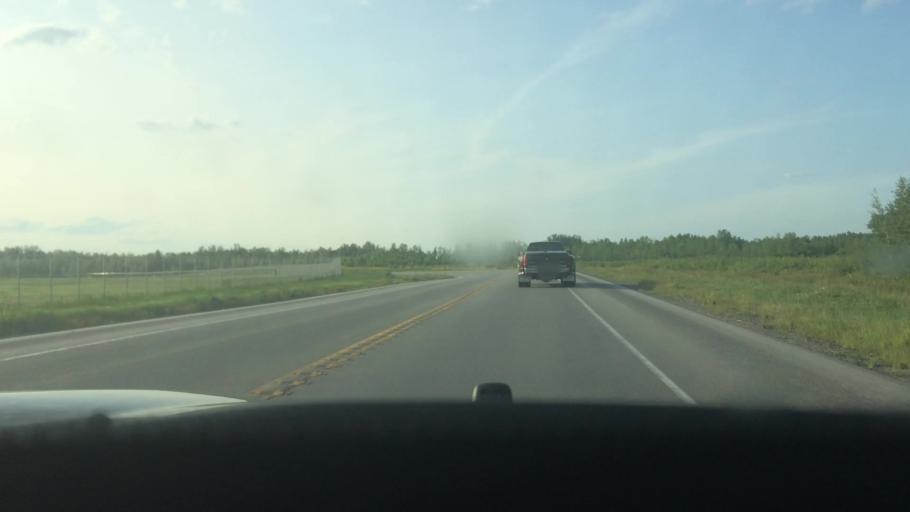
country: US
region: New York
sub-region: St. Lawrence County
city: Ogdensburg
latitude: 44.6831
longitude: -75.4459
